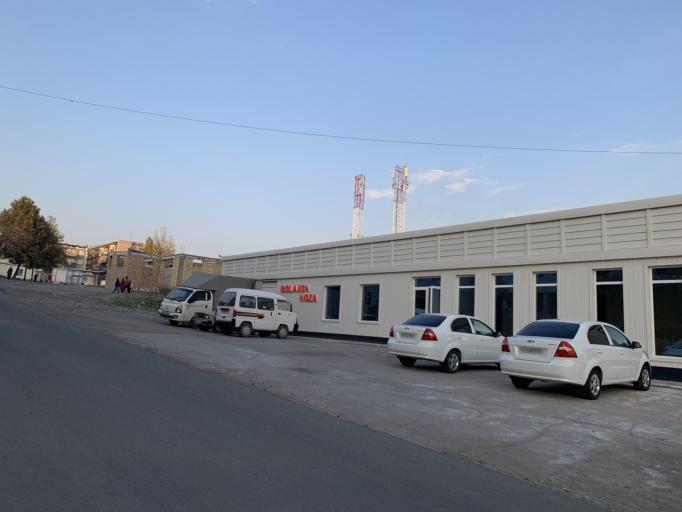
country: UZ
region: Namangan
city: Namangan Shahri
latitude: 41.0039
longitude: 71.5989
